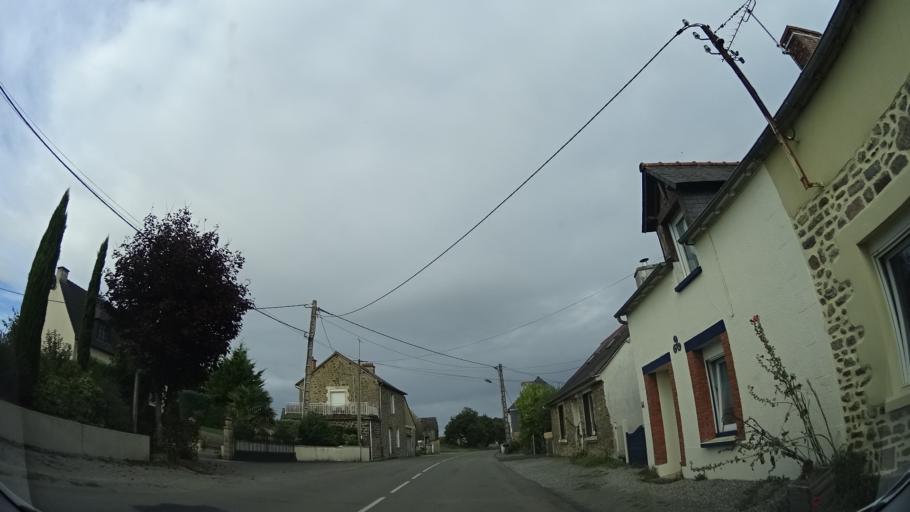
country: FR
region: Brittany
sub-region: Departement d'Ille-et-Vilaine
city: Hede-Bazouges
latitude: 48.2962
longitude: -1.7838
